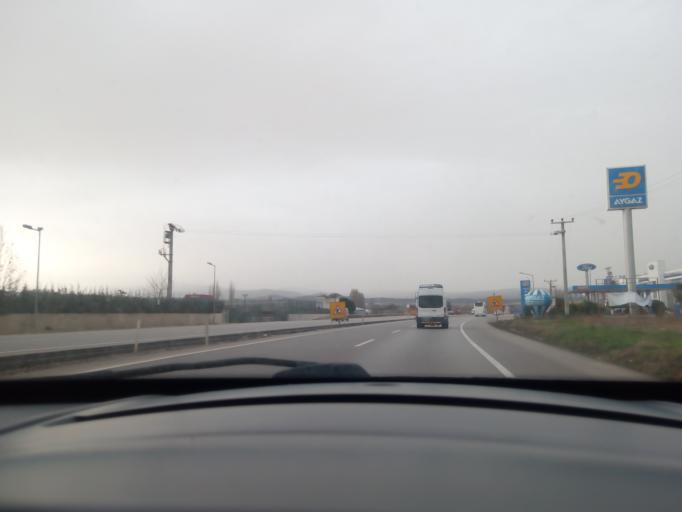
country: TR
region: Bursa
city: Tatkavakli
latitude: 40.0361
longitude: 28.3757
